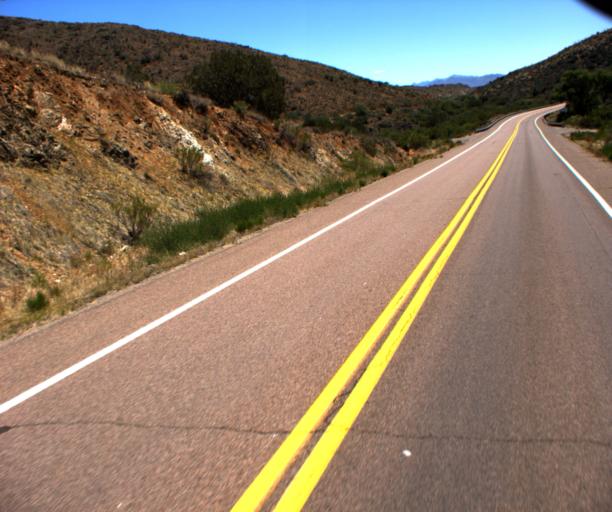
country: US
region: Arizona
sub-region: Yavapai County
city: Bagdad
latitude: 34.5613
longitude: -113.1658
